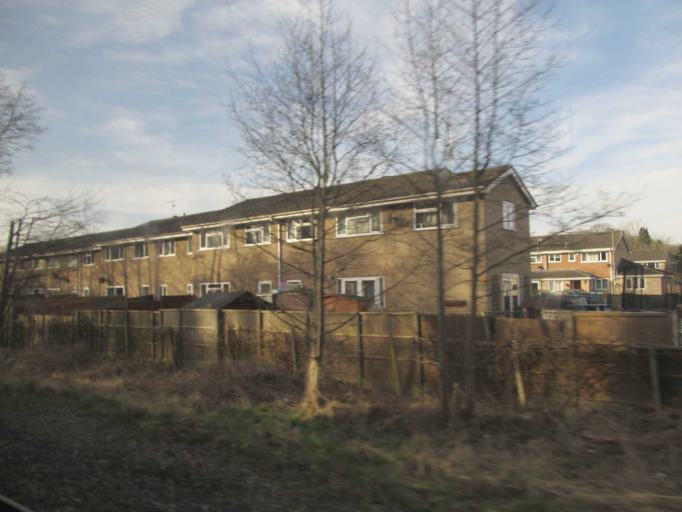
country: GB
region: England
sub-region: Hampshire
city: Farnborough
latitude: 51.2906
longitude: -0.7387
